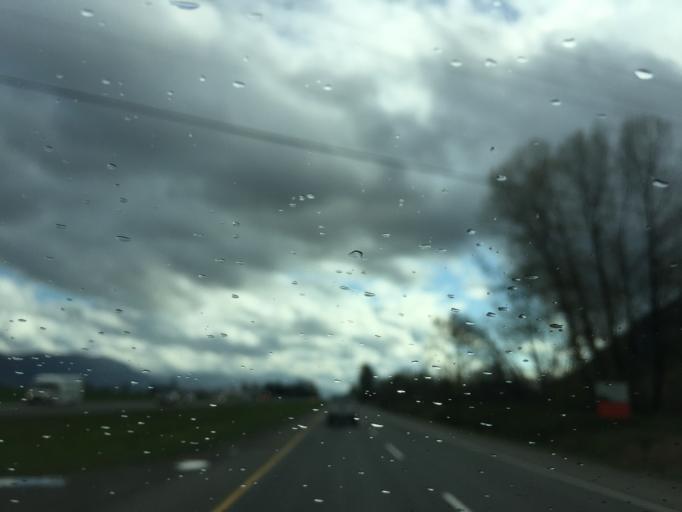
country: CA
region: British Columbia
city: Abbotsford
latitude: 49.1160
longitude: -122.1048
